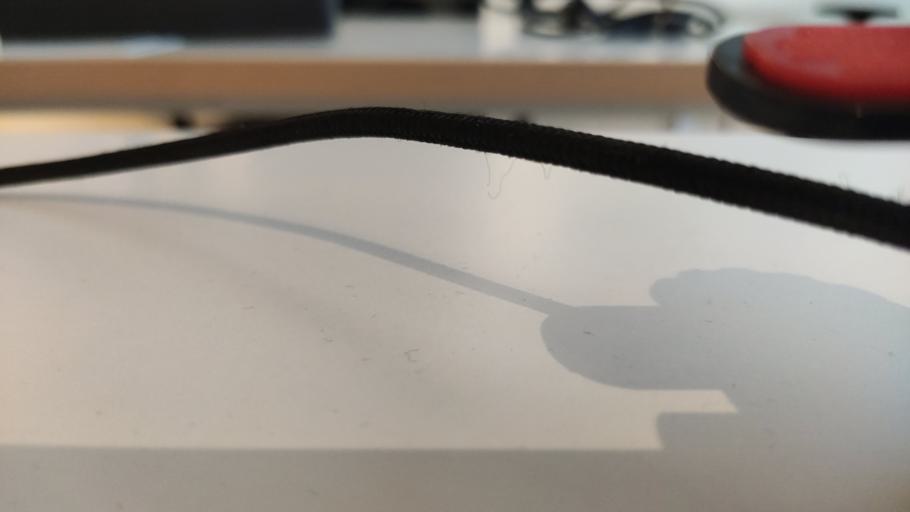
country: RU
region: Moskovskaya
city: Novopetrovskoye
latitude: 55.9473
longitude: 36.4370
